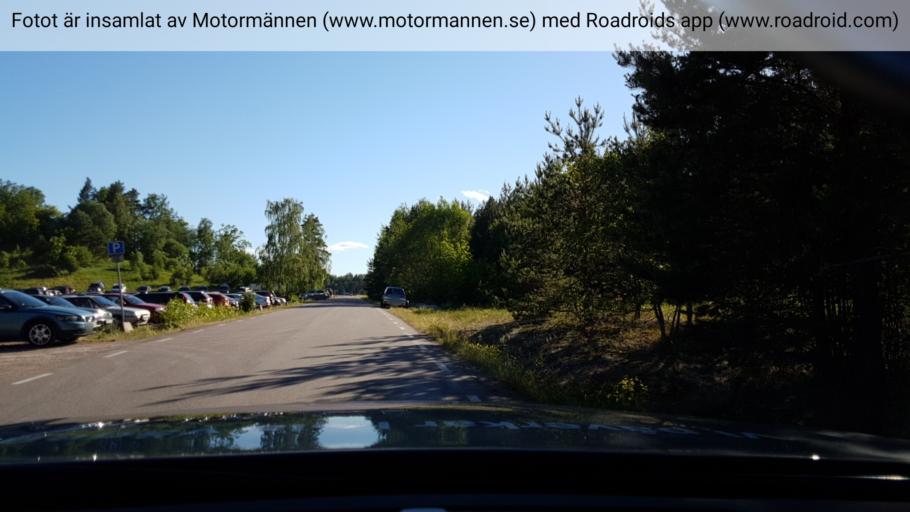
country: SE
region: Vaestmanland
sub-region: Hallstahammars Kommun
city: Kolback
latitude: 59.5452
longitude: 16.2496
